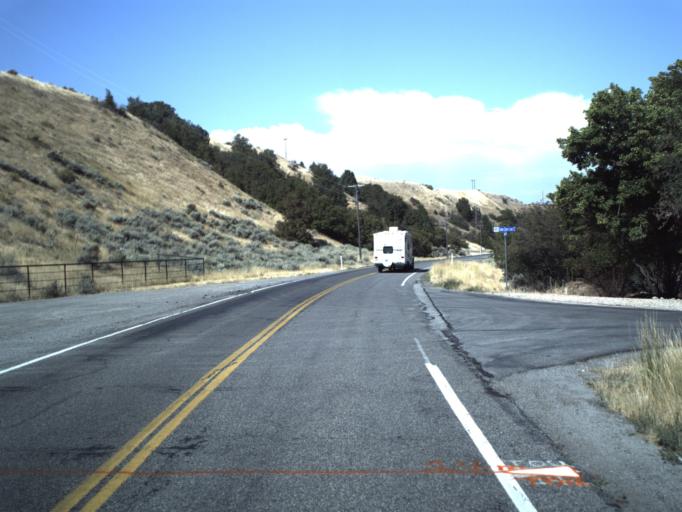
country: US
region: Utah
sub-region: Cache County
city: Hyrum
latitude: 41.6278
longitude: -111.8050
